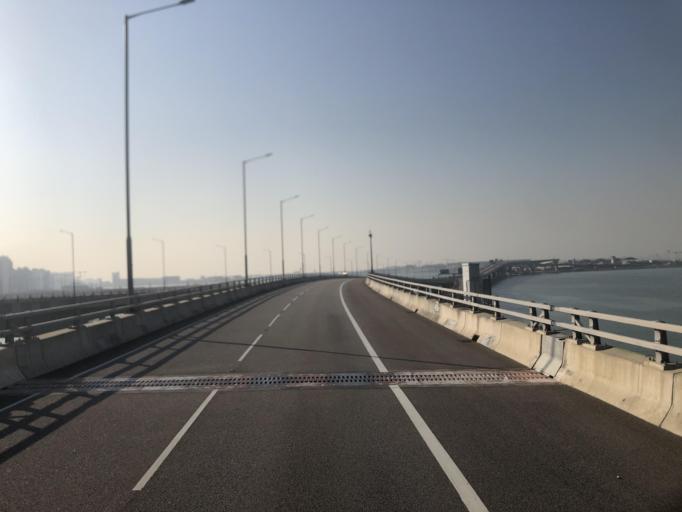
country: HK
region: Tuen Mun
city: Tuen Mun
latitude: 22.3020
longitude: 113.9737
